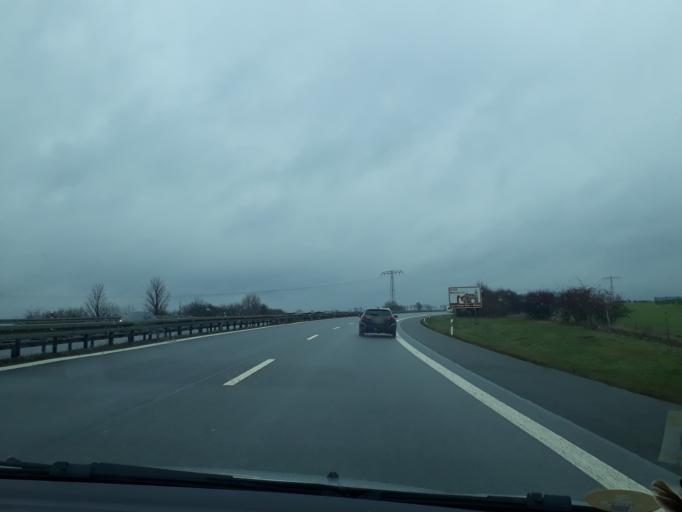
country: DE
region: Saxony
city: Bautzen
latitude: 51.1966
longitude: 14.4242
